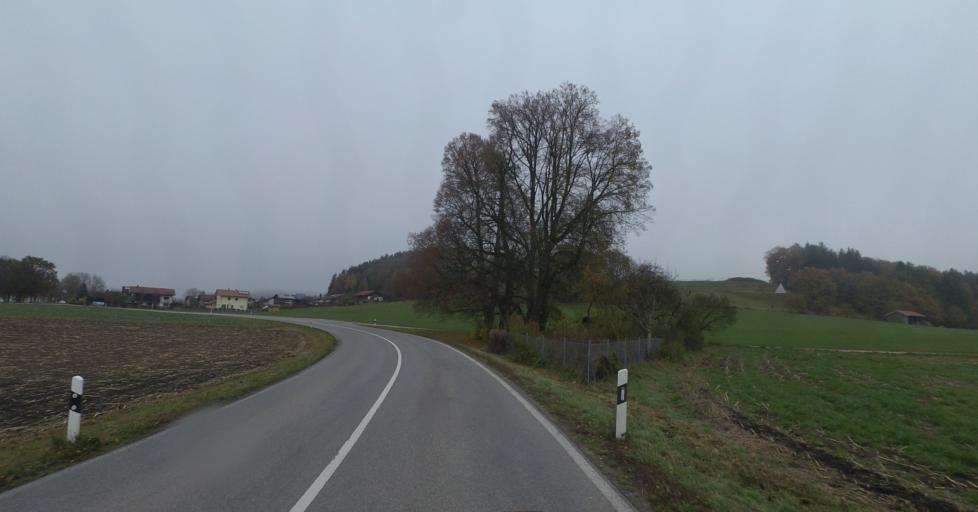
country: DE
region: Bavaria
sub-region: Upper Bavaria
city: Seeon-Seebruck
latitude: 47.9535
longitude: 12.5038
